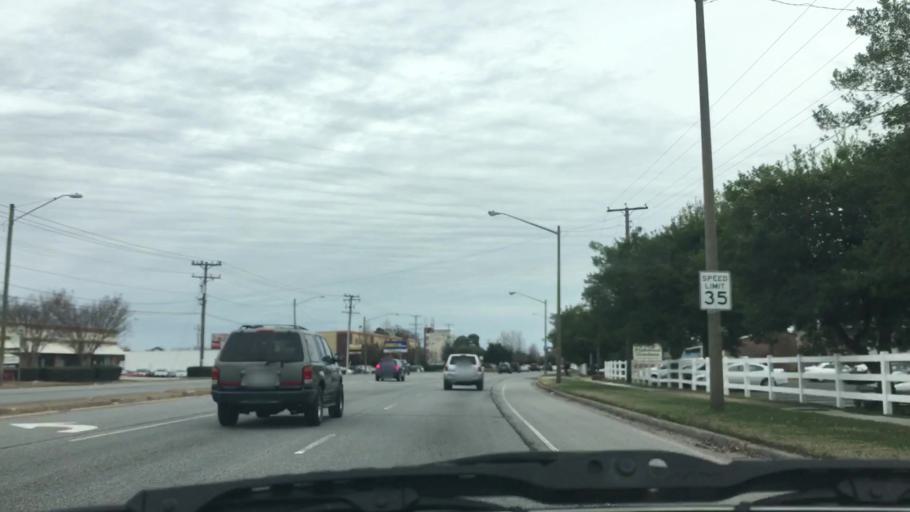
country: US
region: Virginia
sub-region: City of Norfolk
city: Norfolk
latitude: 36.9167
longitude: -76.2289
